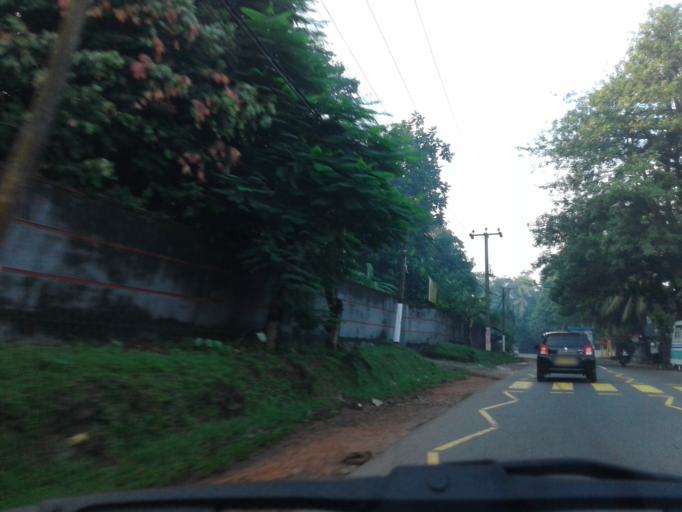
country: LK
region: Western
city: Mulleriyawa
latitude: 6.9560
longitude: 79.9943
